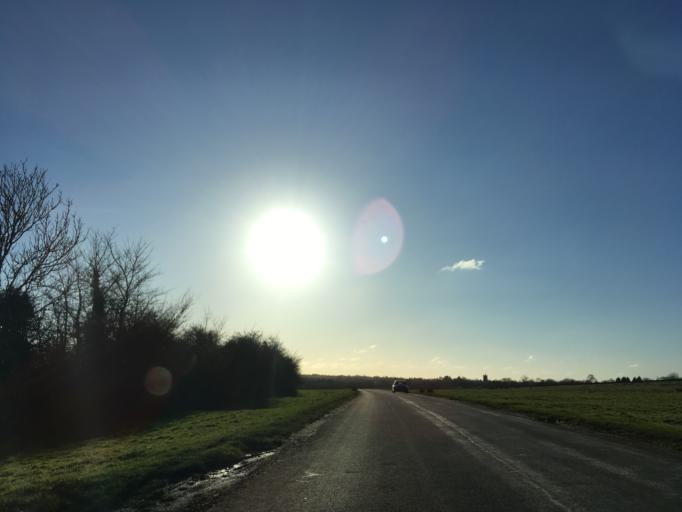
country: GB
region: England
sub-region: South Gloucestershire
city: Chipping Sodbury
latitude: 51.5497
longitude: -2.3790
